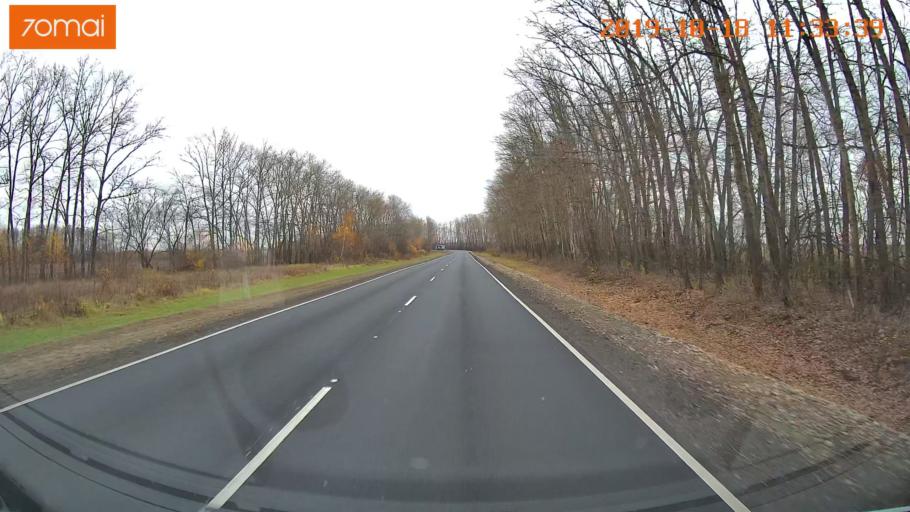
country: RU
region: Rjazan
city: Oktyabr'skiy
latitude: 54.1395
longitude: 38.7462
